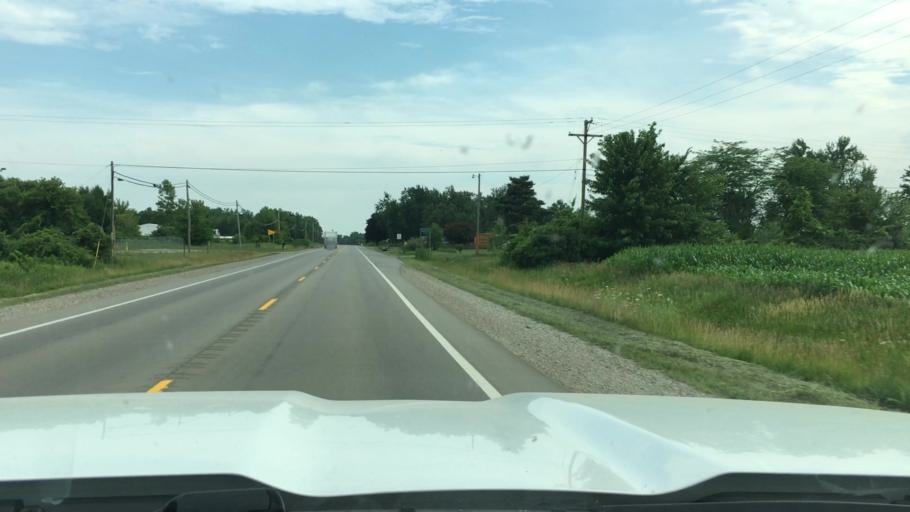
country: US
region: Michigan
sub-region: Sanilac County
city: Marlette
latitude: 43.3500
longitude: -83.0848
